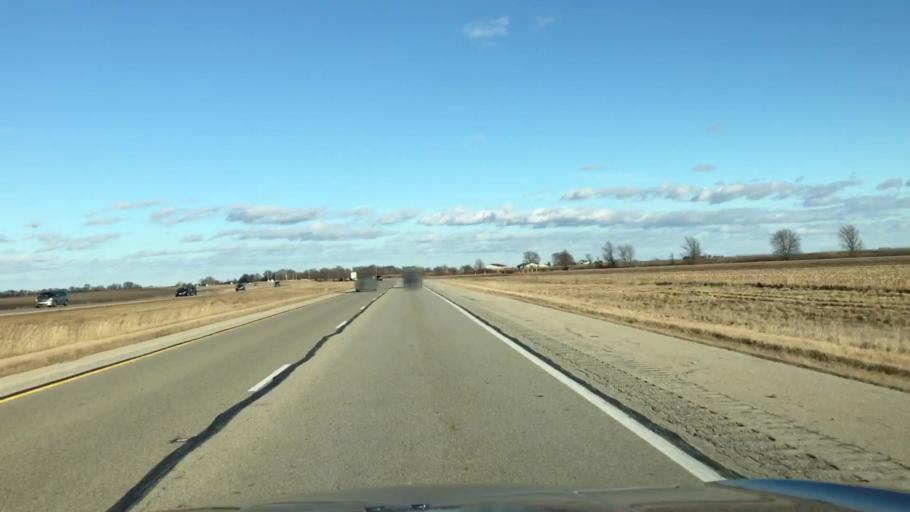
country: US
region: Illinois
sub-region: McLean County
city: Lexington
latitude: 40.5882
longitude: -88.8655
